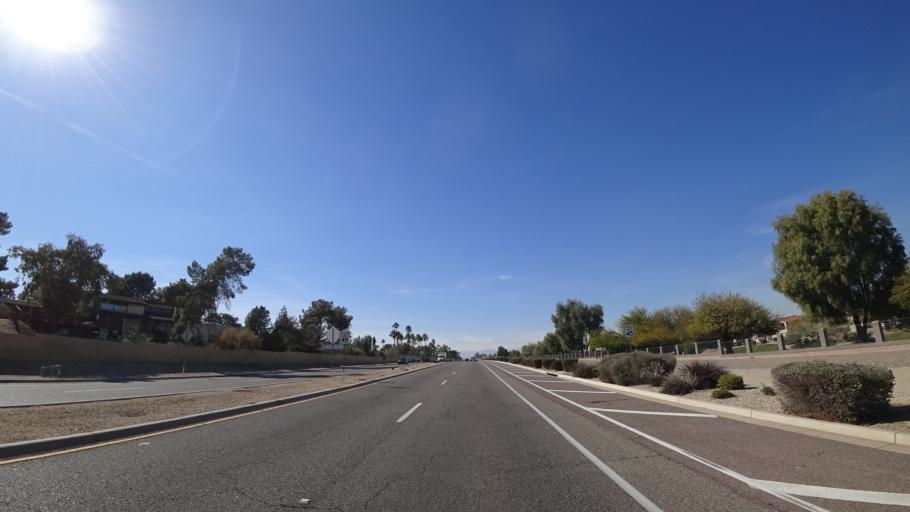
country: US
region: Arizona
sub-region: Maricopa County
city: Litchfield Park
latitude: 33.5081
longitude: -112.3497
